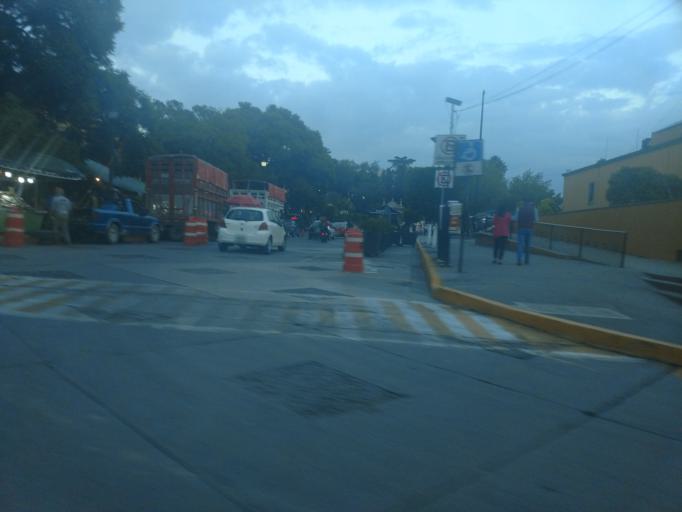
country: MX
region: Mexico
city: Tepotzotlan
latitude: 19.7142
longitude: -99.2240
